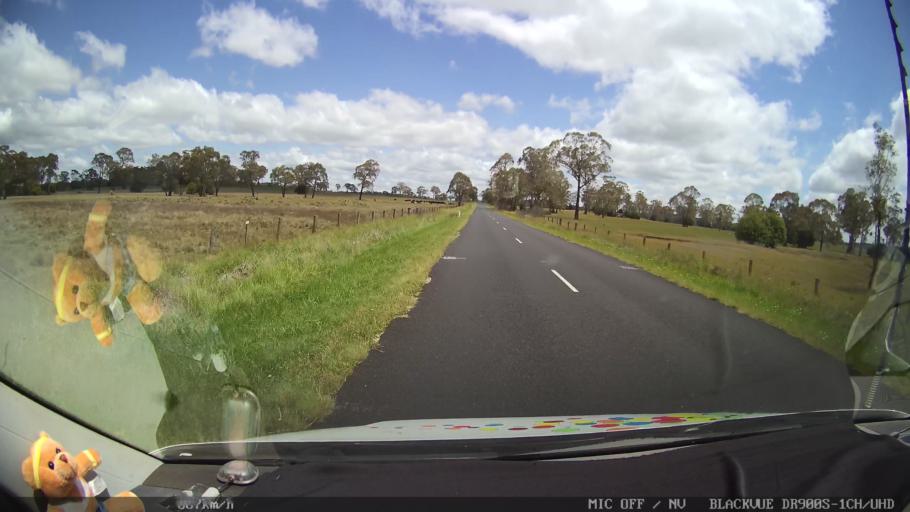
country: AU
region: New South Wales
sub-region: Glen Innes Severn
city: Glen Innes
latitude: -29.6270
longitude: 151.6723
